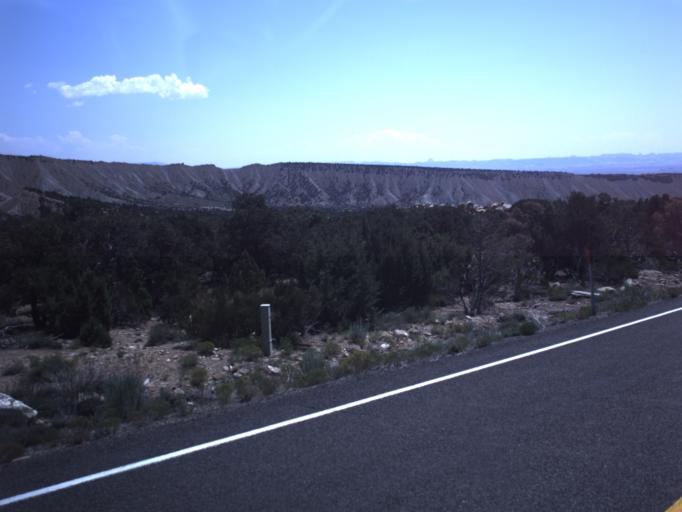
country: US
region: Utah
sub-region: Emery County
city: Orangeville
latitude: 39.2996
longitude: -111.1172
